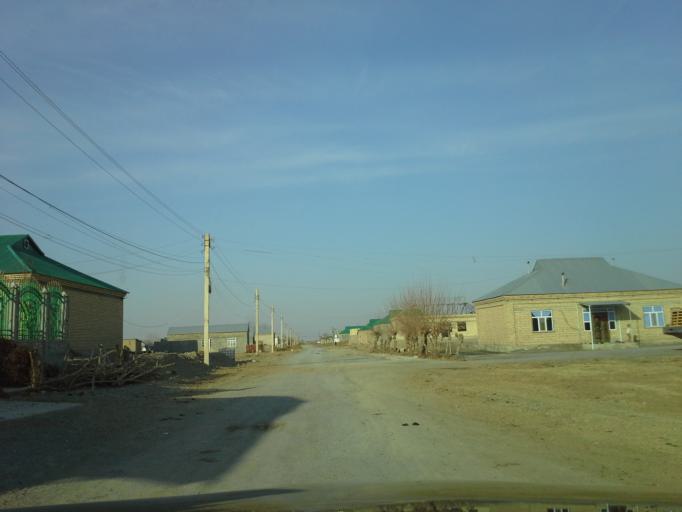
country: TM
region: Ahal
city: Abadan
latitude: 38.1758
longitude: 58.0467
